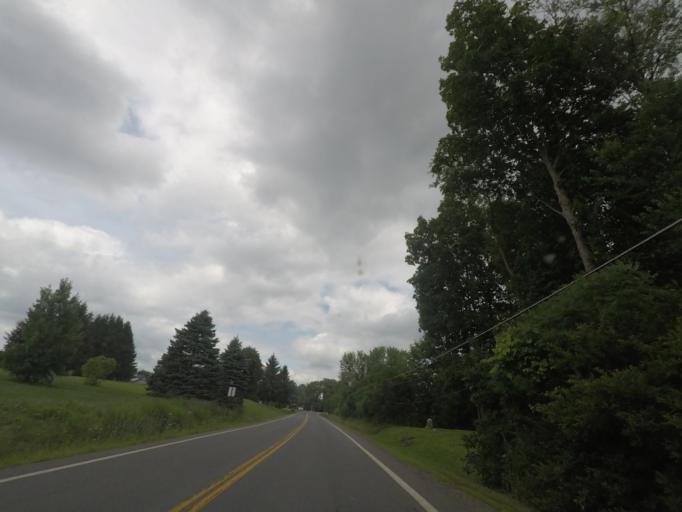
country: US
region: New York
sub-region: Saratoga County
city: Stillwater
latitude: 43.0020
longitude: -73.7073
